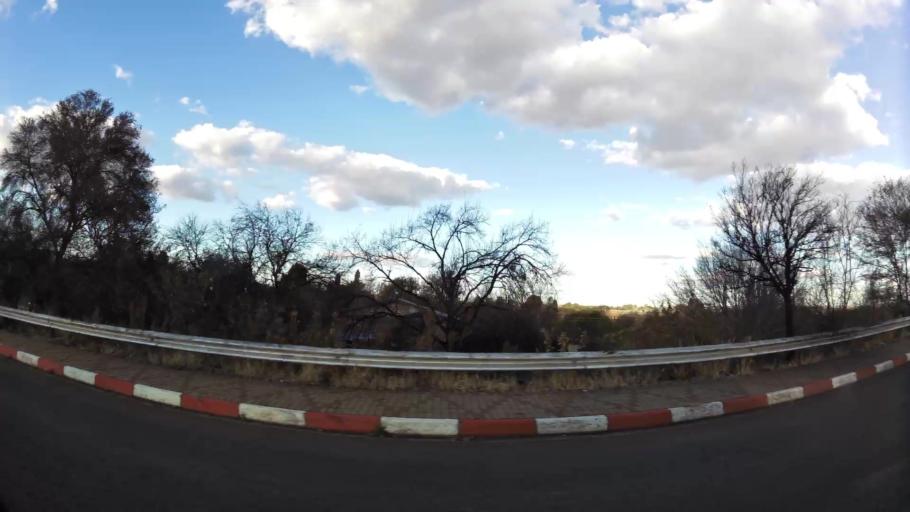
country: ZA
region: North-West
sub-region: Dr Kenneth Kaunda District Municipality
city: Potchefstroom
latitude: -26.6797
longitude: 27.0960
